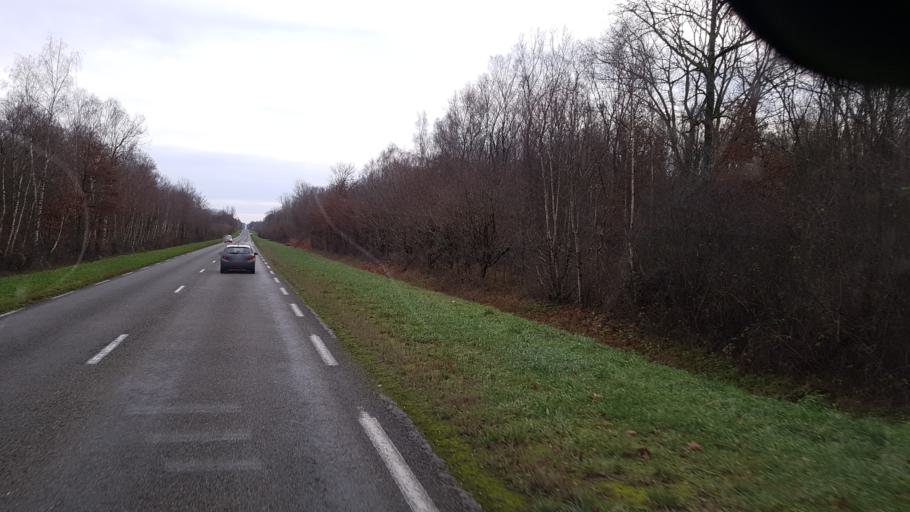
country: FR
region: Centre
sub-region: Departement du Loiret
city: La Ferte-Saint-Aubin
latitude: 47.6981
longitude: 1.9507
